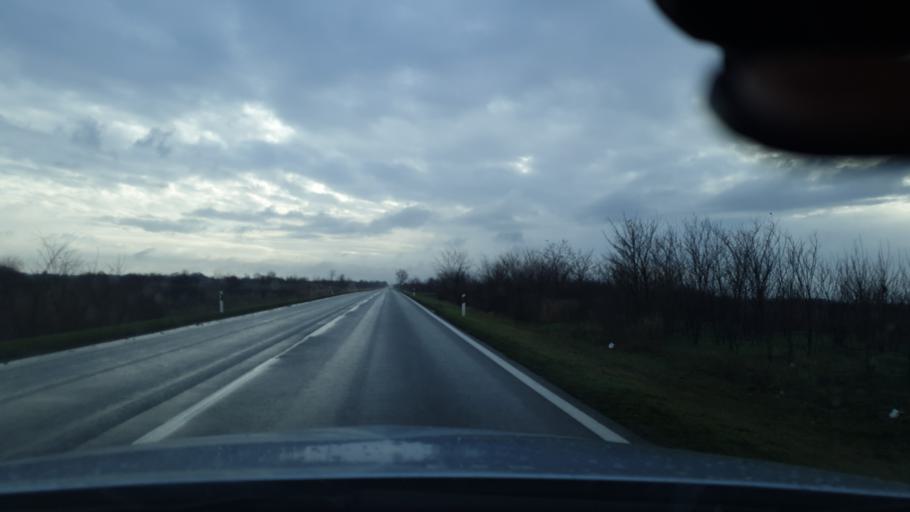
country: RS
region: Autonomna Pokrajina Vojvodina
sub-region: Juznobanatski Okrug
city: Kovin
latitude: 44.7745
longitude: 20.9392
